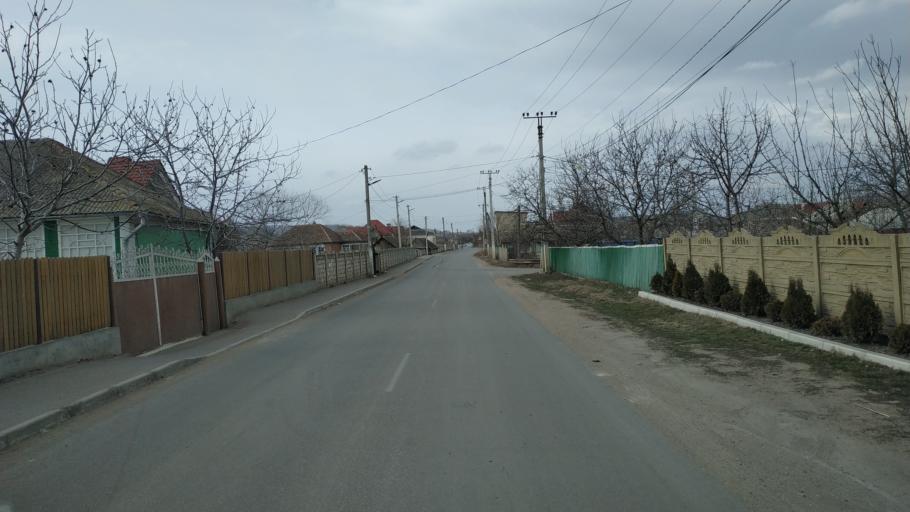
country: MD
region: Laloveni
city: Ialoveni
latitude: 46.8623
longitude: 28.7809
